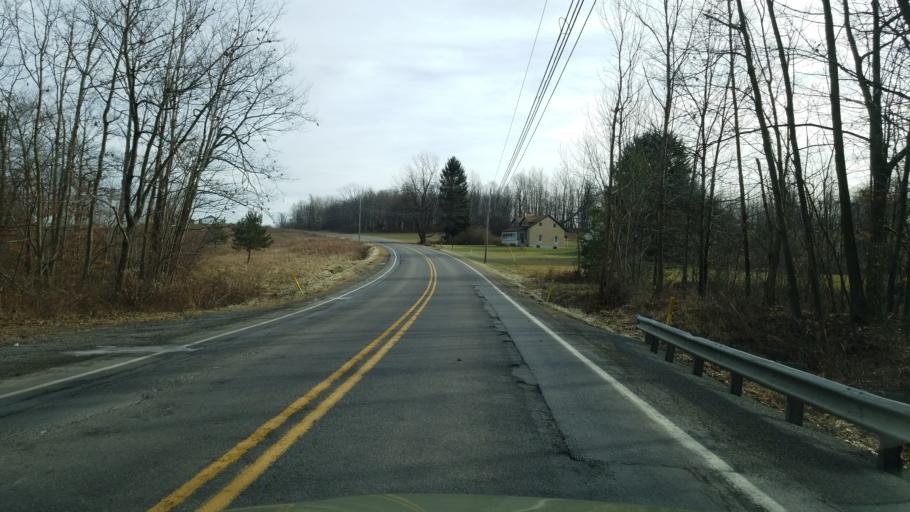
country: US
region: Pennsylvania
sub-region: Indiana County
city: Johnsonburg
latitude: 40.9162
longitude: -78.8438
